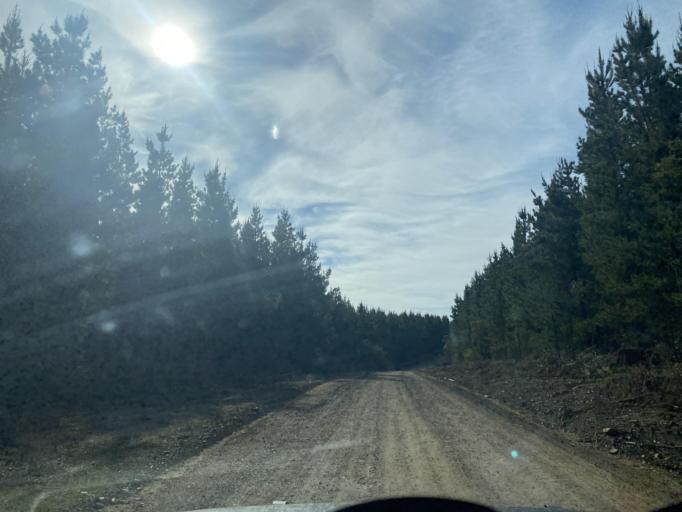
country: AU
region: Victoria
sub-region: Mansfield
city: Mansfield
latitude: -36.8770
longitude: 146.1857
